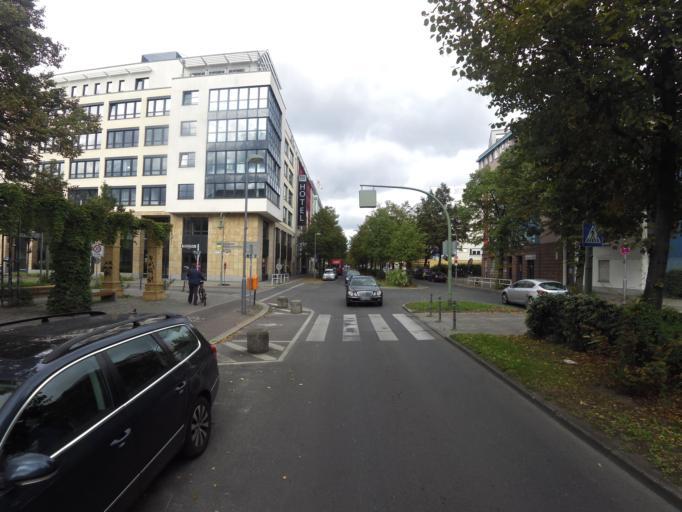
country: DE
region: Berlin
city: Bezirk Kreuzberg
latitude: 52.5012
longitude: 13.3863
